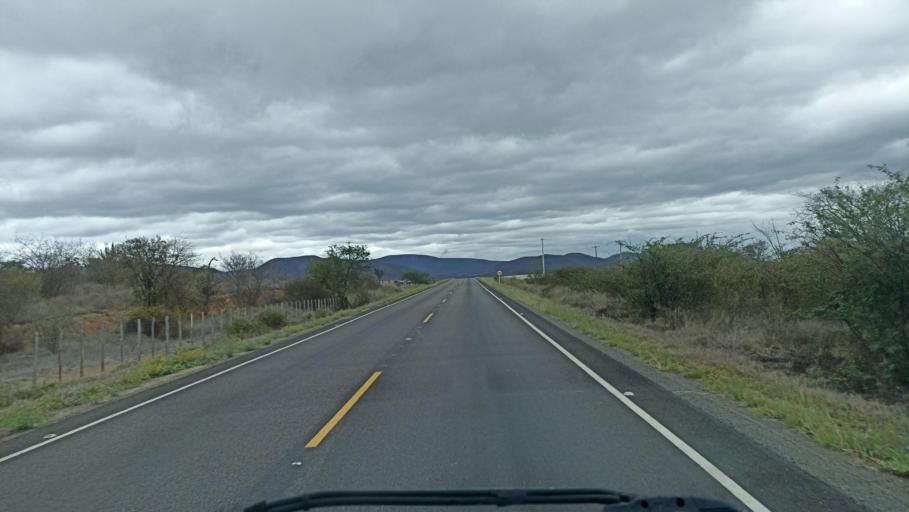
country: BR
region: Bahia
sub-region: Iacu
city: Iacu
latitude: -12.9140
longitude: -40.4105
